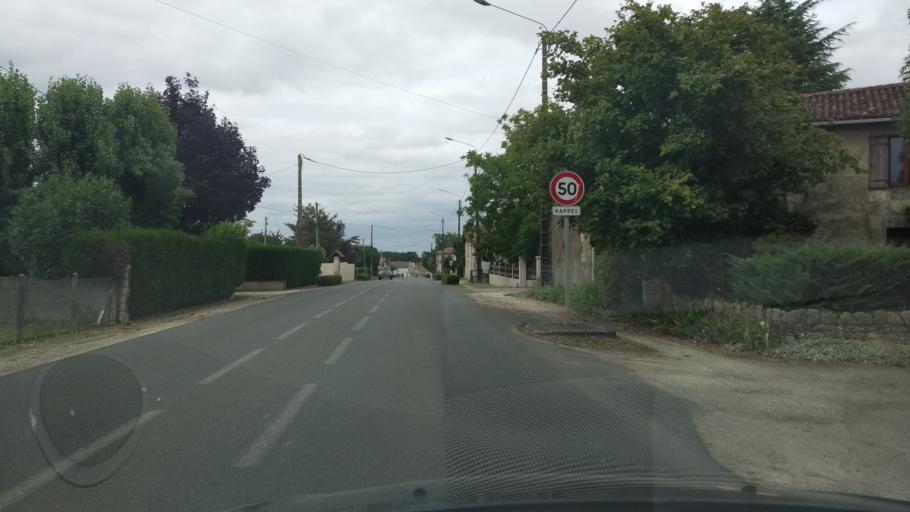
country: FR
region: Poitou-Charentes
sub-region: Departement de la Vienne
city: La Villedieu-du-Clain
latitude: 46.4506
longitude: 0.3680
